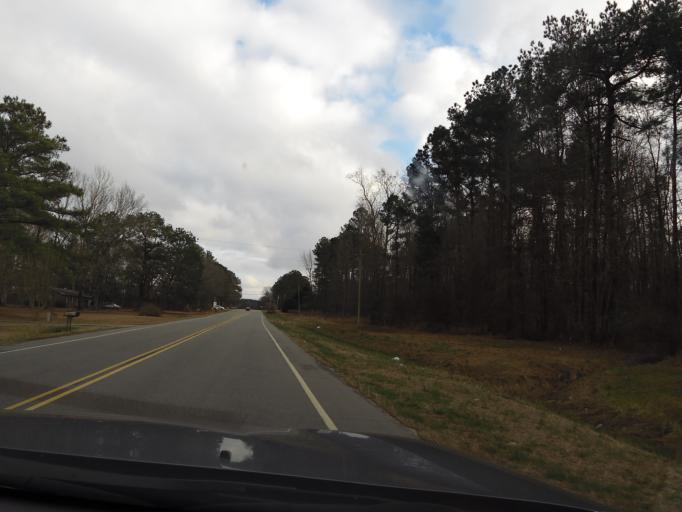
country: US
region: North Carolina
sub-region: Edgecombe County
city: Pinetops
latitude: 35.8036
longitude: -77.6435
